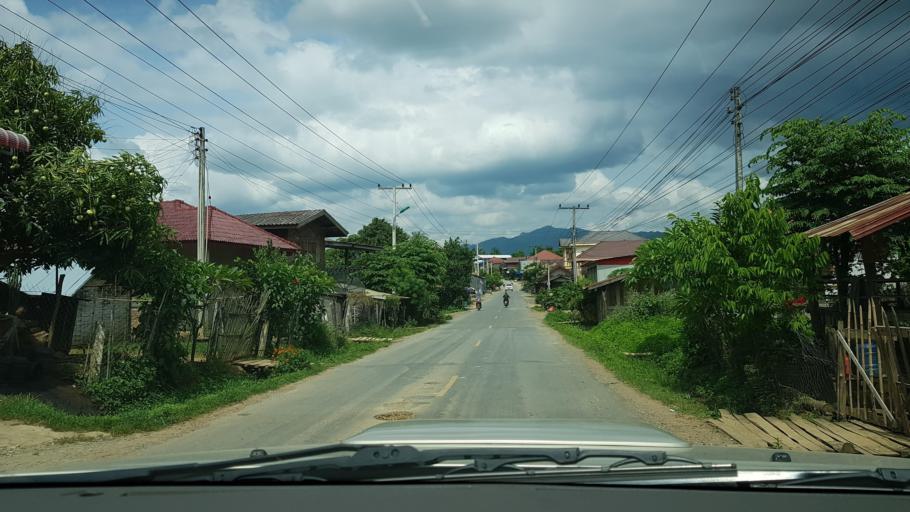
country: LA
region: Loungnamtha
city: Muang Nale
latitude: 20.1265
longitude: 101.4346
